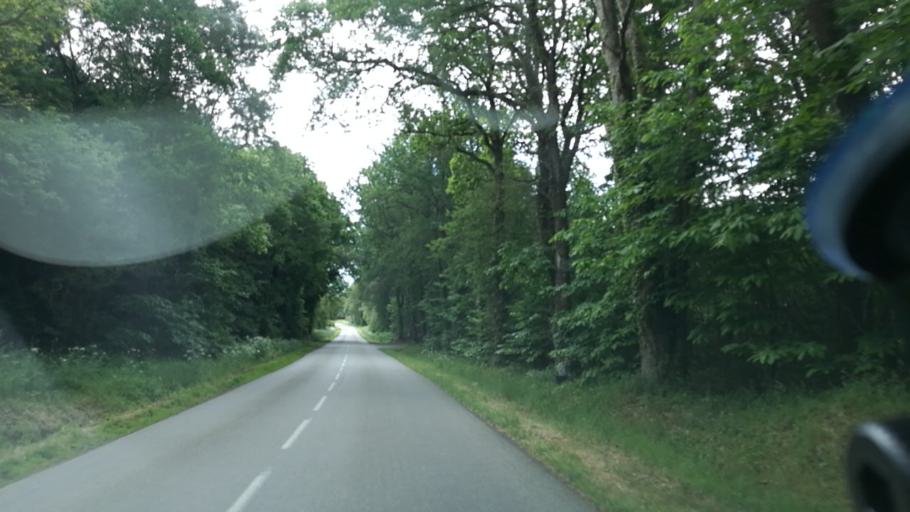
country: FR
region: Brittany
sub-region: Departement du Morbihan
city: Penestin
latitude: 47.4756
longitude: -2.4338
